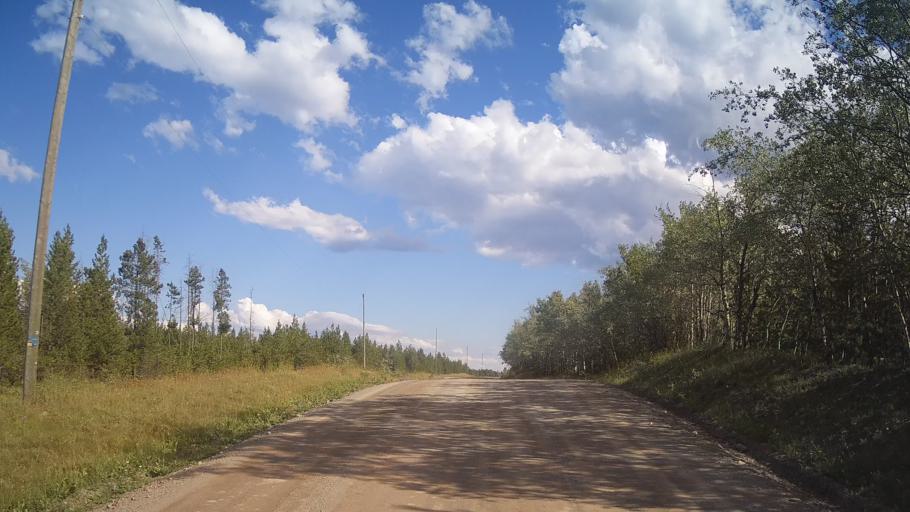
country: CA
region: British Columbia
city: Cache Creek
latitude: 51.2811
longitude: -121.7372
